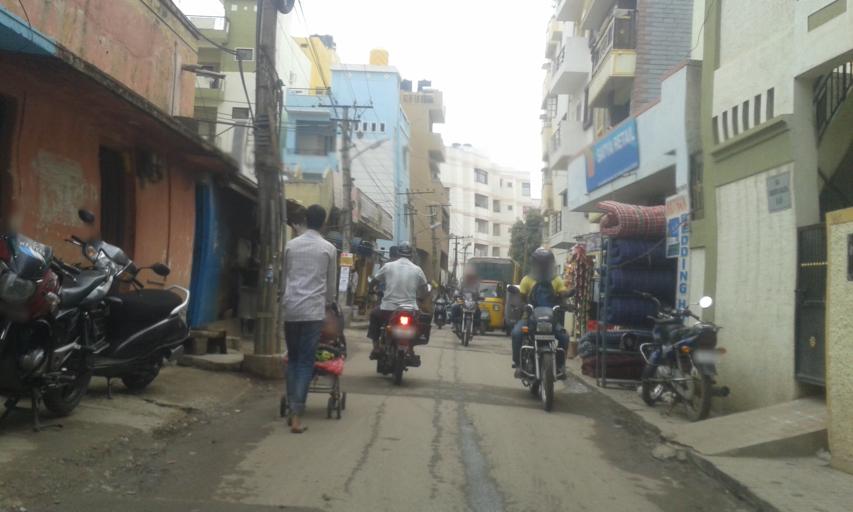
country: IN
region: Karnataka
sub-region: Bangalore Urban
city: Bangalore
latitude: 12.9629
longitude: 77.6471
